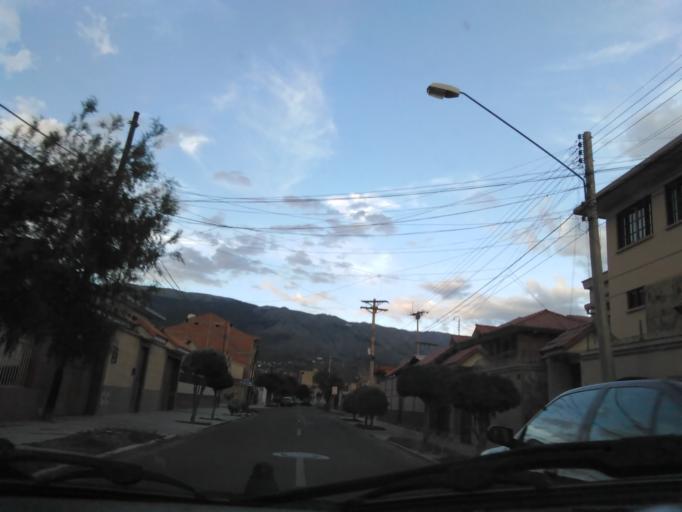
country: BO
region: Cochabamba
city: Cochabamba
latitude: -17.3842
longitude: -66.1660
